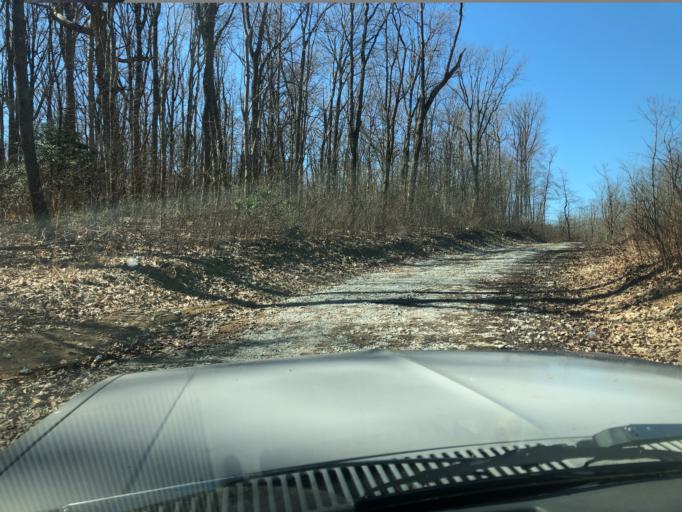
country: US
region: Tennessee
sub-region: Roane County
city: Rockwood
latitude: 35.9788
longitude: -84.7466
